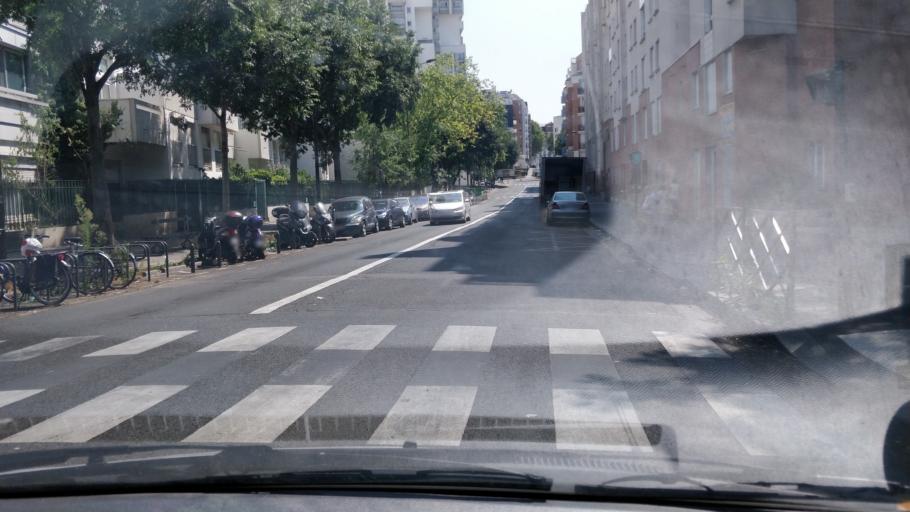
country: FR
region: Ile-de-France
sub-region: Departement de Seine-Saint-Denis
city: Bagnolet
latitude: 48.8561
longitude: 2.4057
